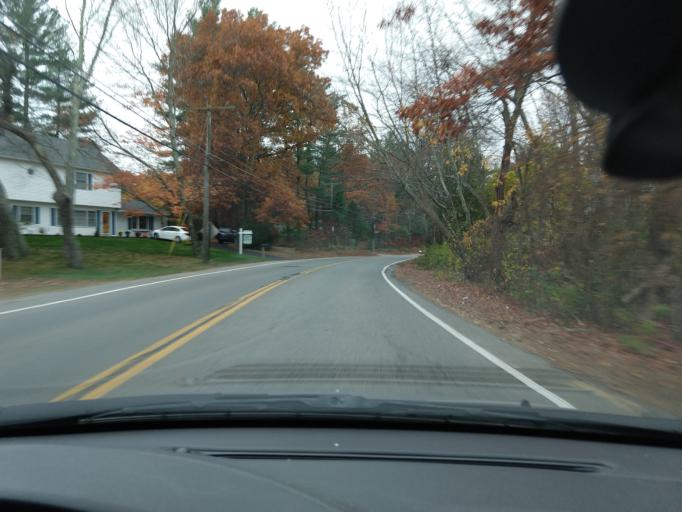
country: US
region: Massachusetts
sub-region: Middlesex County
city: Chelmsford
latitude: 42.5749
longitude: -71.3455
